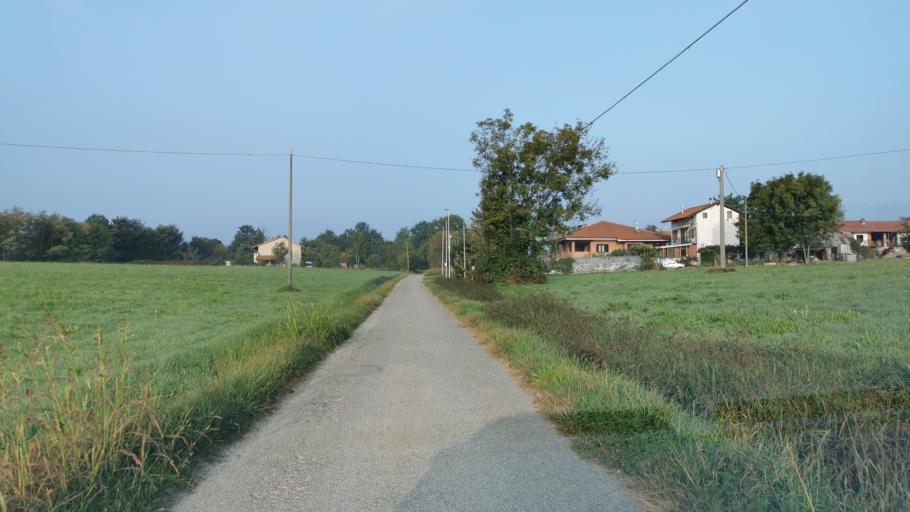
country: IT
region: Piedmont
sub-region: Provincia di Torino
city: Front
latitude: 45.2550
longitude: 7.6697
